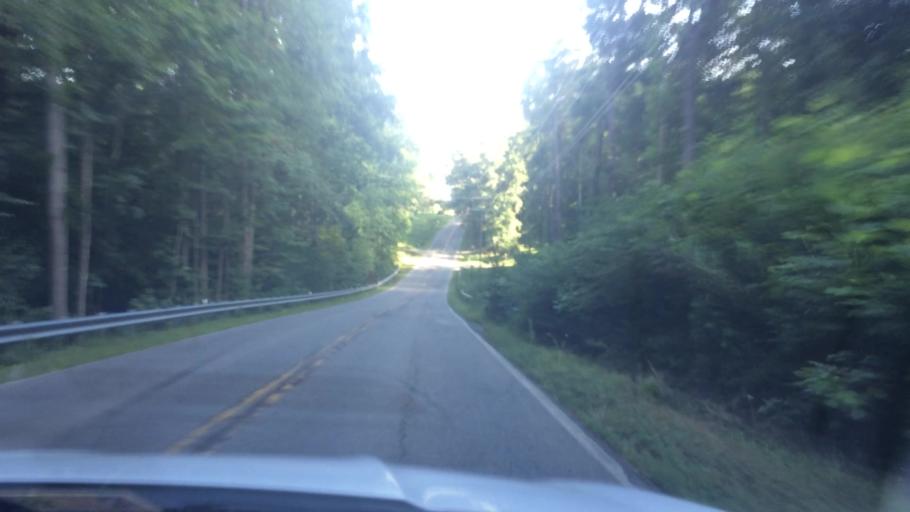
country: US
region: Virginia
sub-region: Middlesex County
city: Deltaville
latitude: 37.5648
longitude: -76.4521
